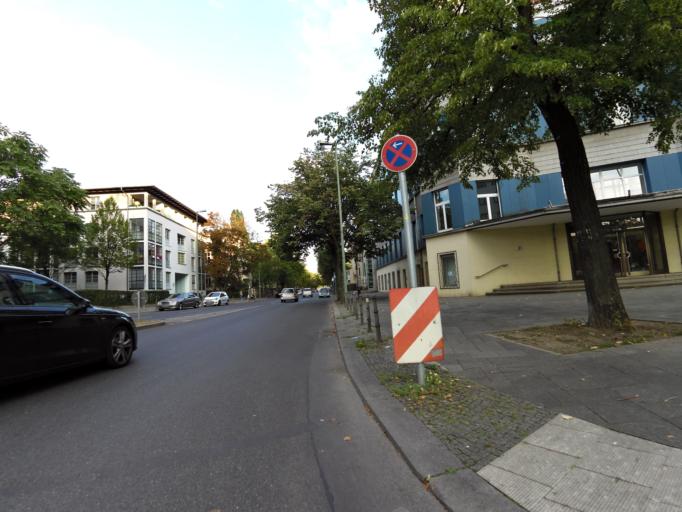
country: DE
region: Berlin
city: Berlin Schoeneberg
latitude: 52.5021
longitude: 13.3534
